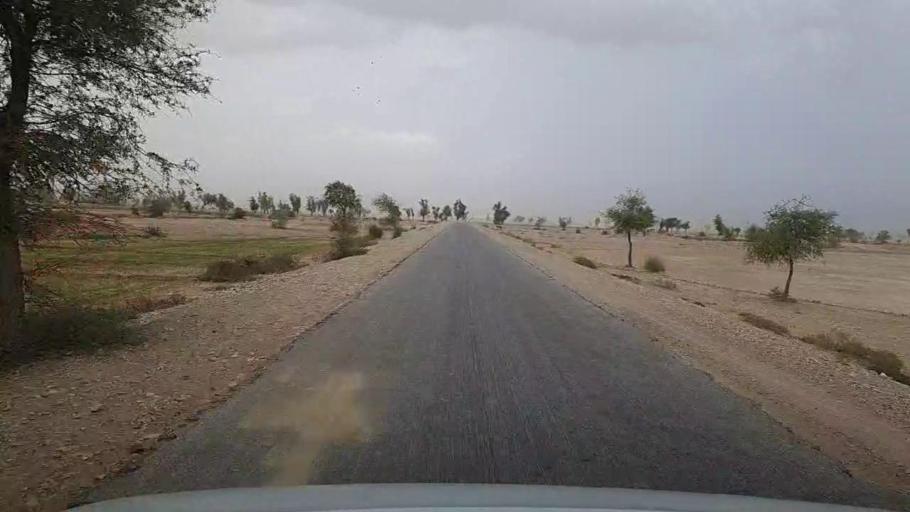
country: PK
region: Sindh
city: Sehwan
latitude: 26.3200
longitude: 67.7290
